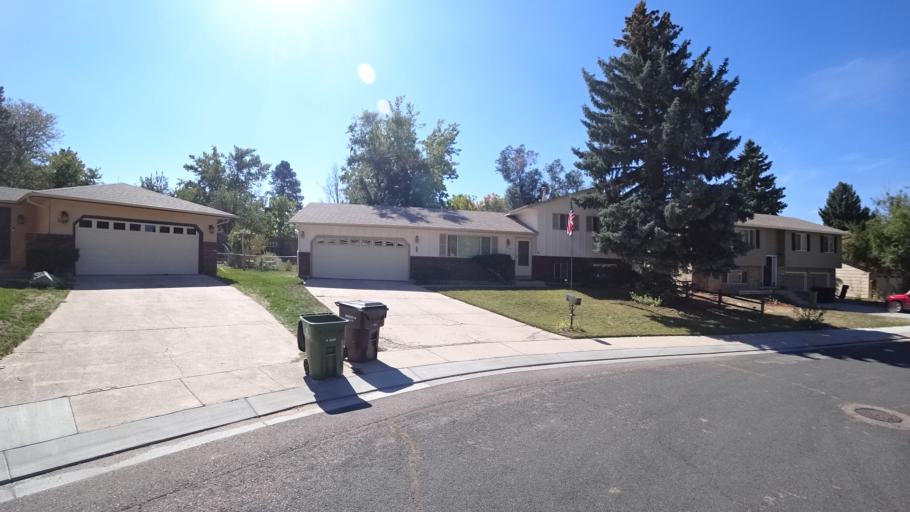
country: US
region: Colorado
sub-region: El Paso County
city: Cimarron Hills
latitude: 38.9125
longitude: -104.7721
